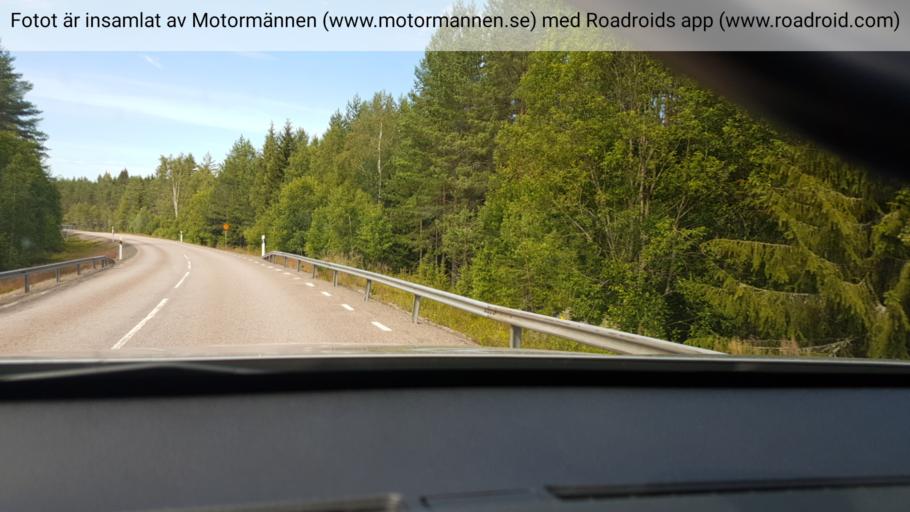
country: SE
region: Vaermland
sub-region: Munkfors Kommun
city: Munkfors
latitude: 59.8725
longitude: 13.3938
